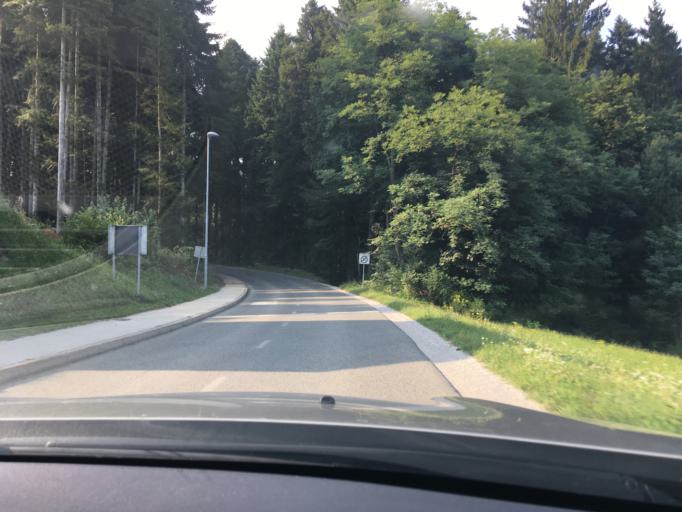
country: SI
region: Dolenjske Toplice
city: Dolenjske Toplice
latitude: 45.7582
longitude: 15.0541
